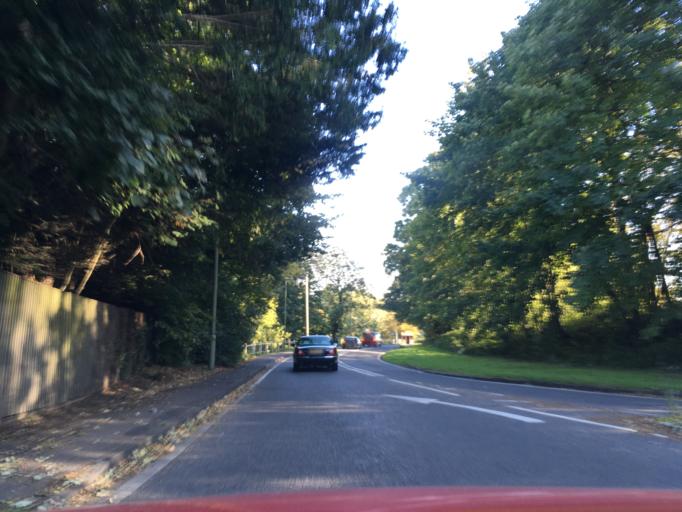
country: GB
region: England
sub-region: Hampshire
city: Swanmore
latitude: 50.9782
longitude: -1.1319
